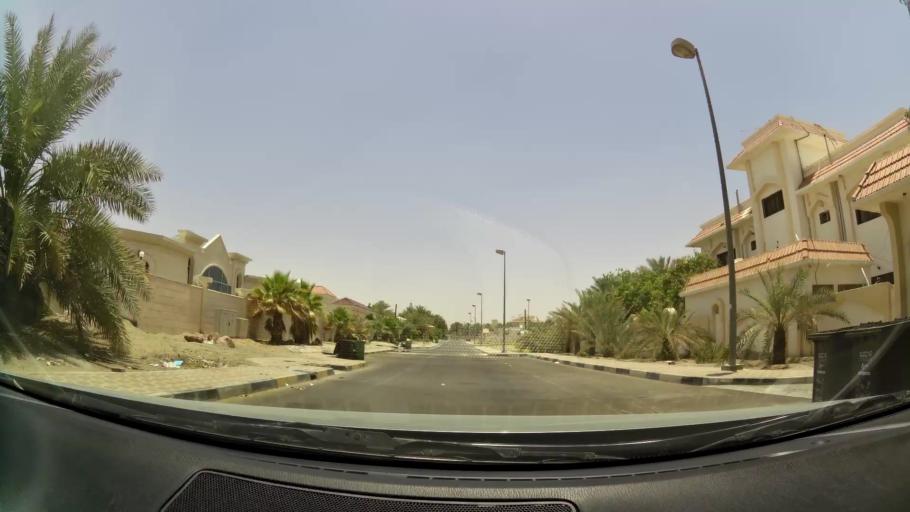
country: OM
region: Al Buraimi
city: Al Buraymi
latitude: 24.2698
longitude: 55.7238
